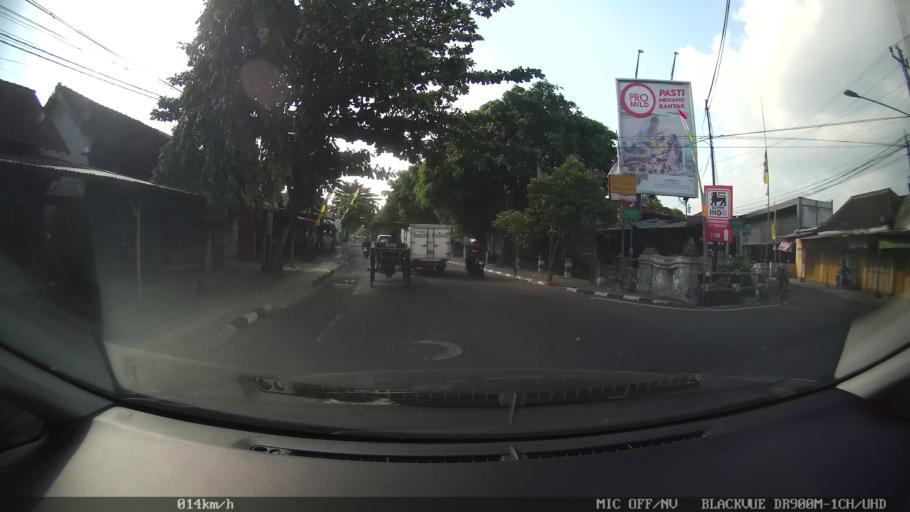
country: ID
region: Daerah Istimewa Yogyakarta
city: Yogyakarta
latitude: -7.8237
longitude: 110.3903
